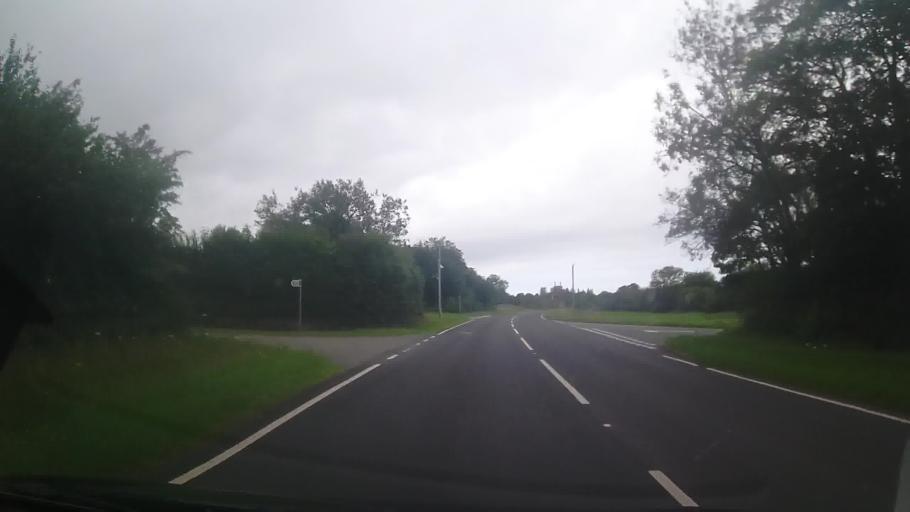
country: GB
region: Wales
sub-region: Gwynedd
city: Caernarfon
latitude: 53.1652
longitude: -4.3134
